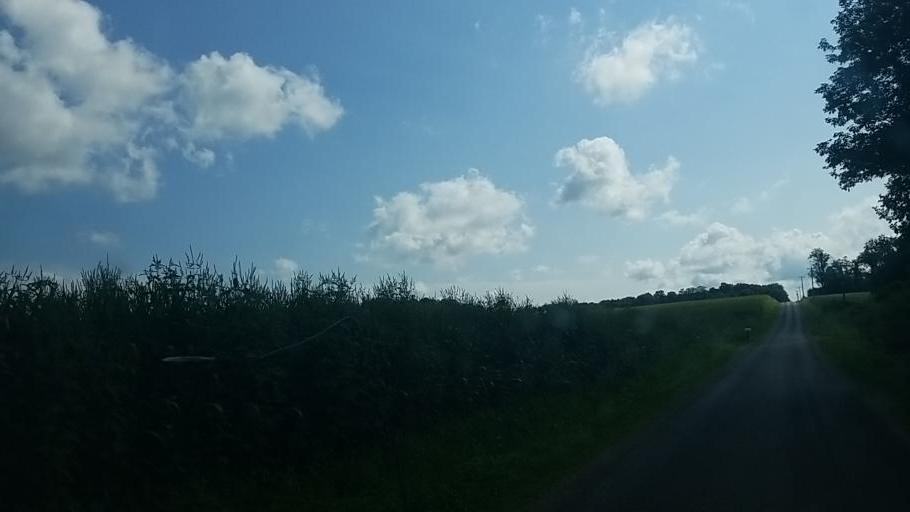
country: US
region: Ohio
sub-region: Ashland County
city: Ashland
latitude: 40.7988
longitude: -82.3370
